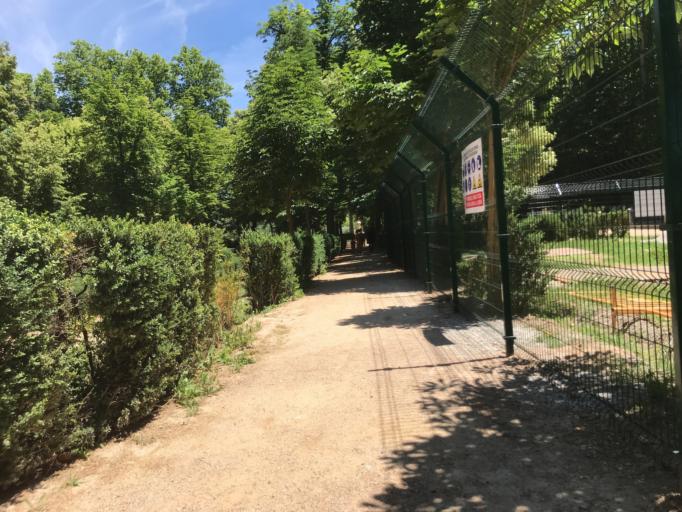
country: ES
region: Madrid
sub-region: Provincia de Madrid
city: Aranjuez
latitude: 40.0374
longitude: -3.6089
